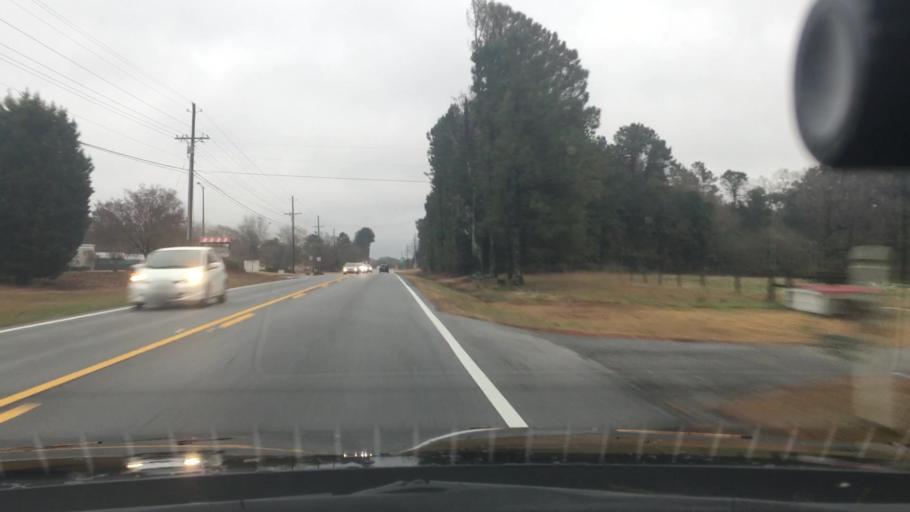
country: US
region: Georgia
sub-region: Fayette County
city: Peachtree City
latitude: 33.3872
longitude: -84.6744
